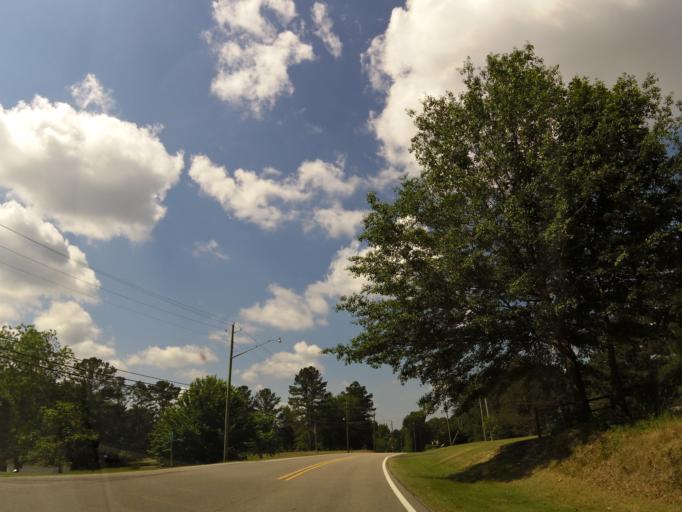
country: US
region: Alabama
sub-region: Marion County
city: Guin
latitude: 33.9773
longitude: -87.8989
